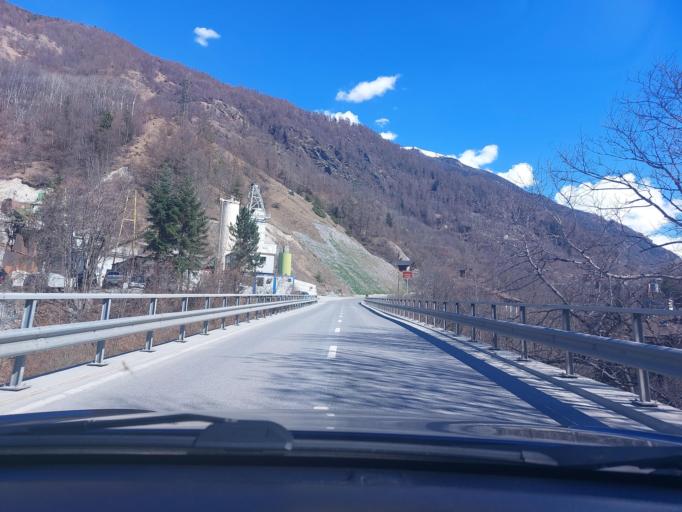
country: CH
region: Valais
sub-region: Herens District
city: Heremence
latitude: 46.1570
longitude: 7.4454
